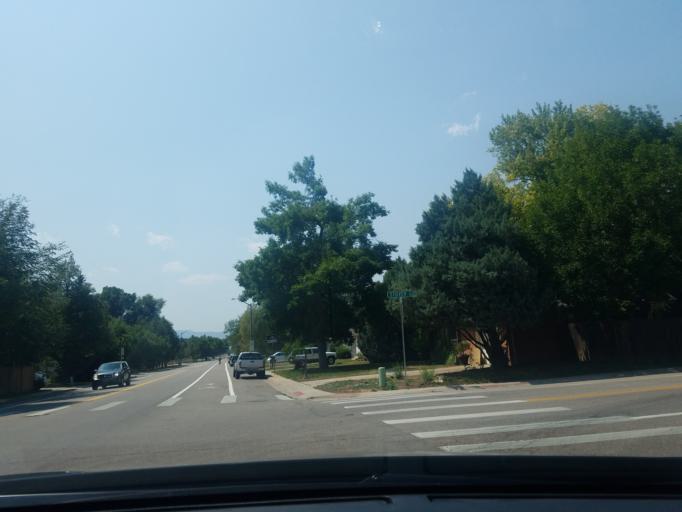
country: US
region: Colorado
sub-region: Larimer County
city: Fort Collins
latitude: 40.5635
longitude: -105.0674
